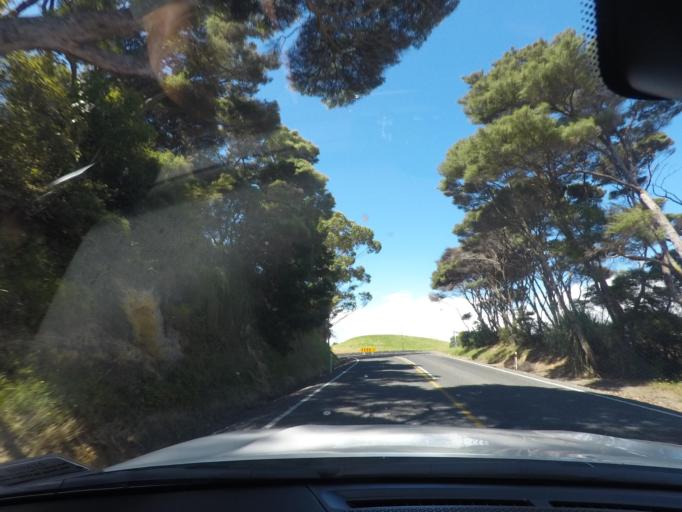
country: NZ
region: Auckland
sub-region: Auckland
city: Parakai
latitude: -36.5951
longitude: 174.3379
